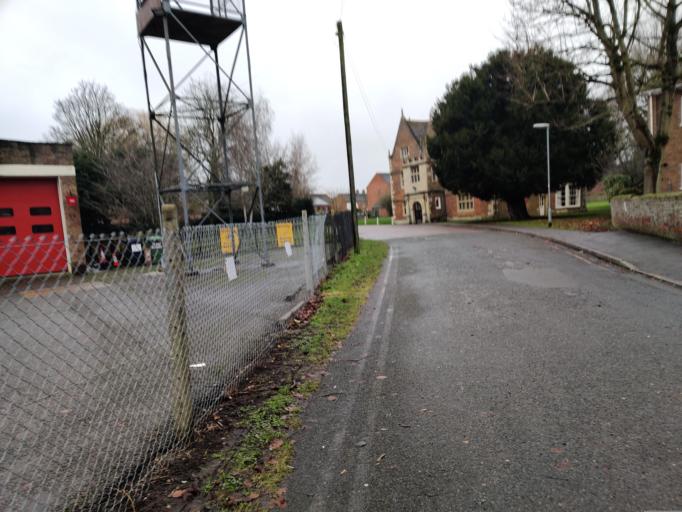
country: GB
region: England
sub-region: Lincolnshire
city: Bourne
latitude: 52.7653
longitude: -0.3764
